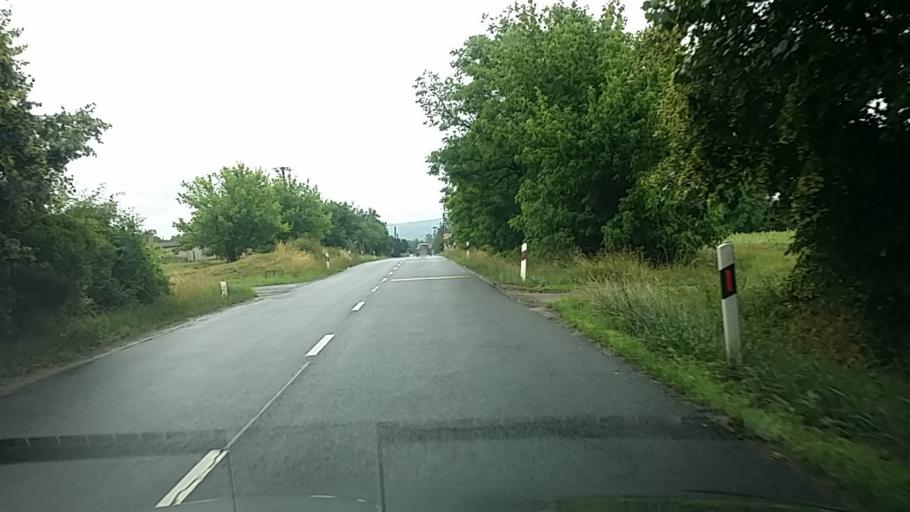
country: HU
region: Komarom-Esztergom
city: Esztergom
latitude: 47.8904
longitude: 18.7758
